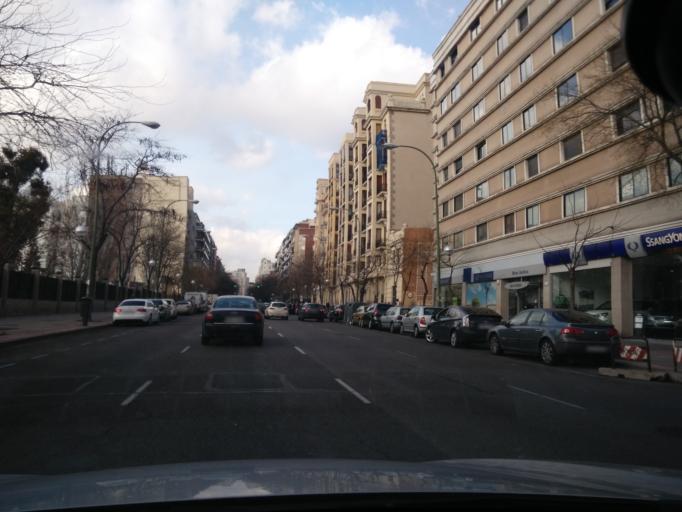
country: ES
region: Madrid
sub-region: Provincia de Madrid
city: Chamberi
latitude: 40.4406
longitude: -3.7012
